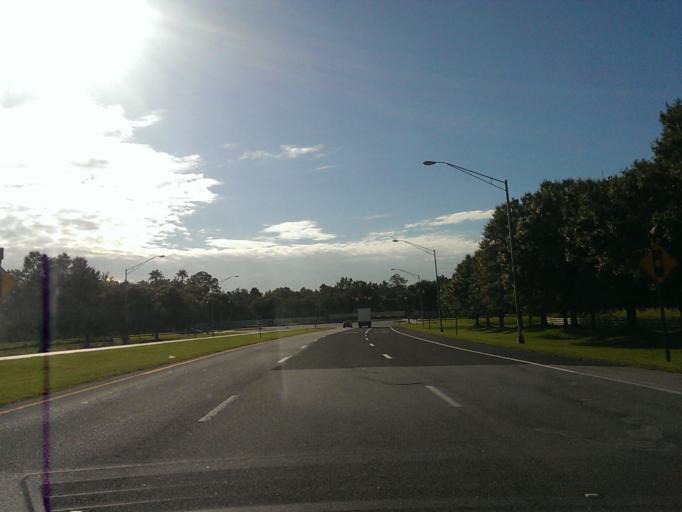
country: US
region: Florida
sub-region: Osceola County
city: Celebration
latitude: 28.3028
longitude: -81.5669
